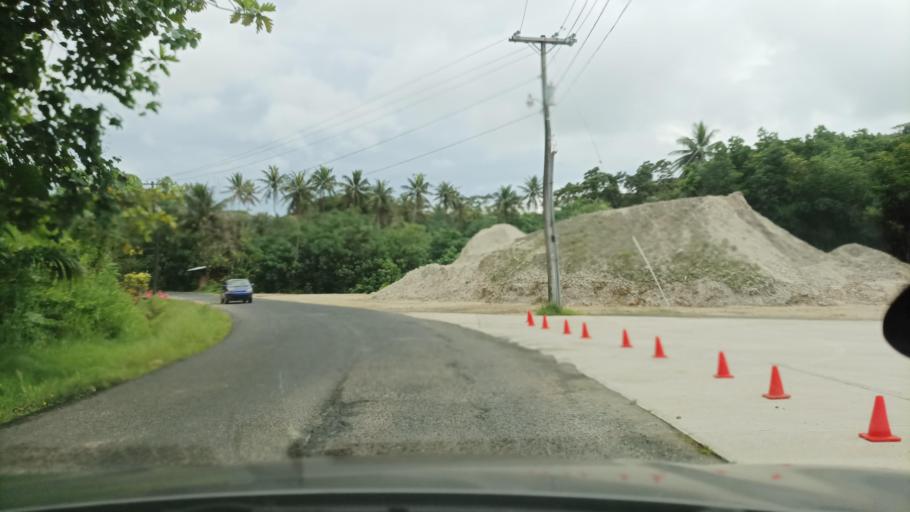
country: FM
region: Pohnpei
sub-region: Kolonia Municipality
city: Kolonia
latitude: 6.9530
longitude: 158.2396
